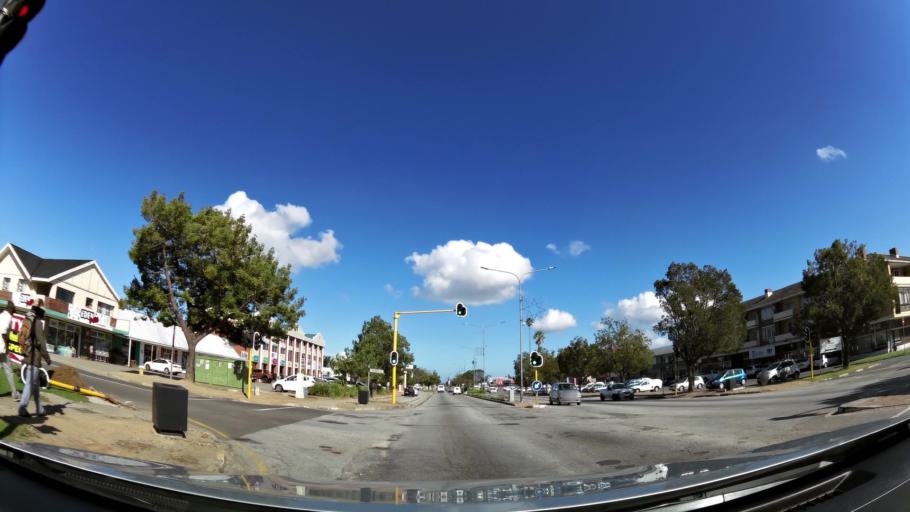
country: ZA
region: Western Cape
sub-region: Eden District Municipality
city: George
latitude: -33.9619
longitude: 22.4544
